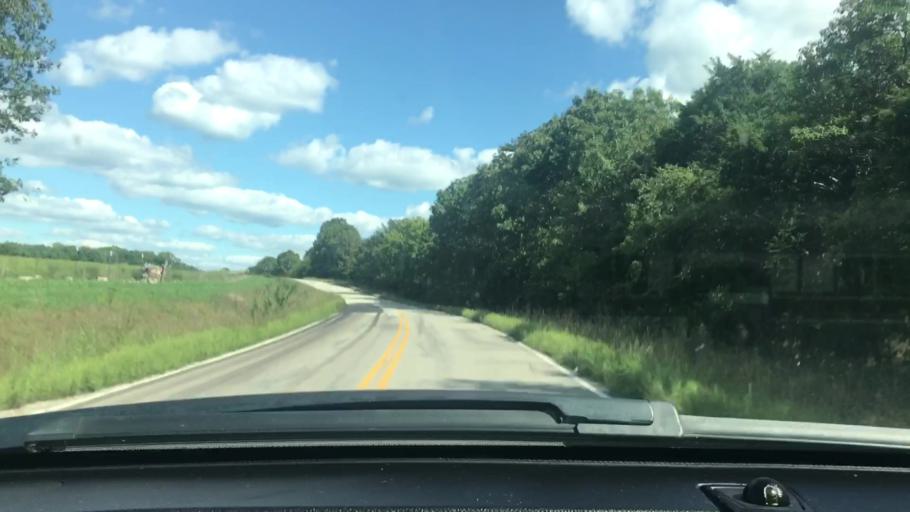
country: US
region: Missouri
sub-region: Wright County
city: Hartville
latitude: 37.3777
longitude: -92.4326
